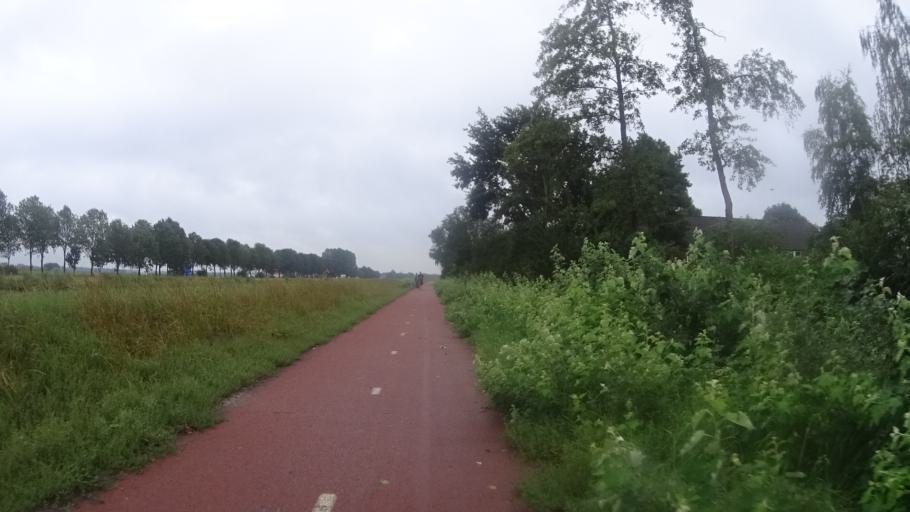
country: NL
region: Groningen
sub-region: Gemeente  Oldambt
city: Winschoten
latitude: 53.1602
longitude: 7.0320
